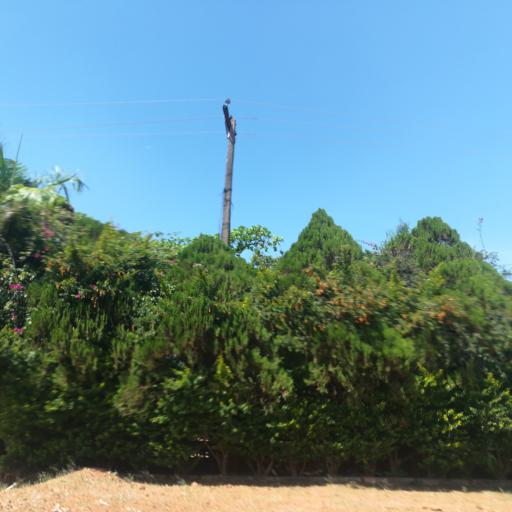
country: NG
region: Plateau
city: Bukuru
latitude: 9.8043
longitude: 8.8698
